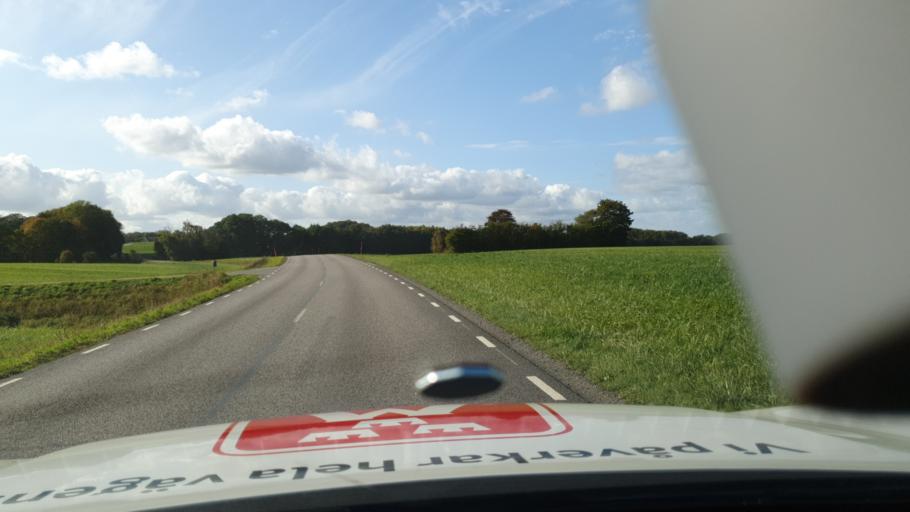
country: SE
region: Skane
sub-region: Sjobo Kommun
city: Sjoebo
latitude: 55.6172
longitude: 13.8128
